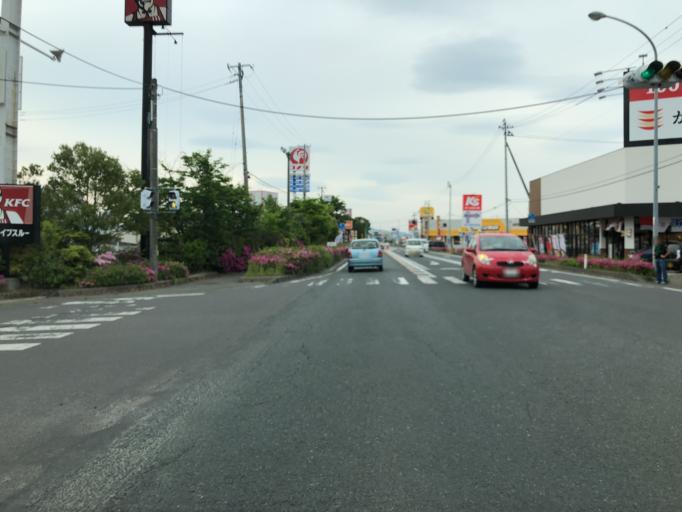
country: JP
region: Miyagi
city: Marumori
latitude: 37.7875
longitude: 140.9323
